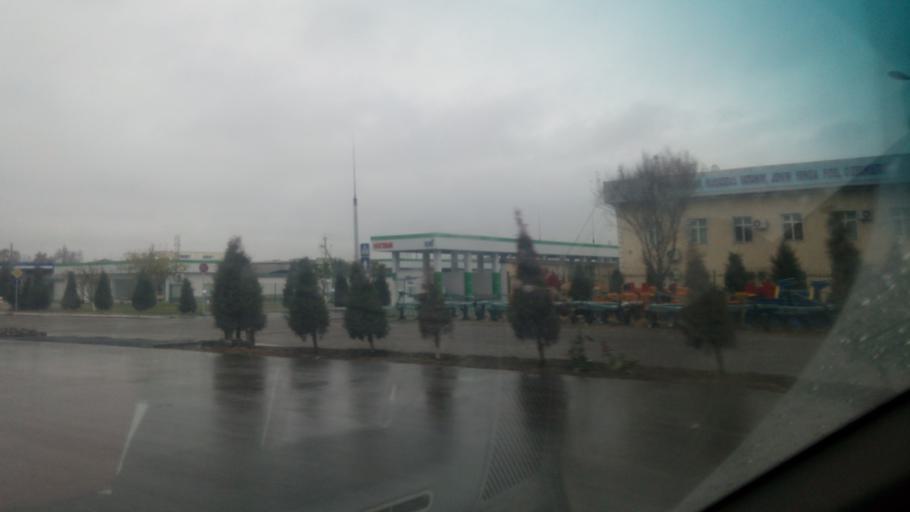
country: UZ
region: Toshkent
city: Urtaowul
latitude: 41.2309
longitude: 69.1524
